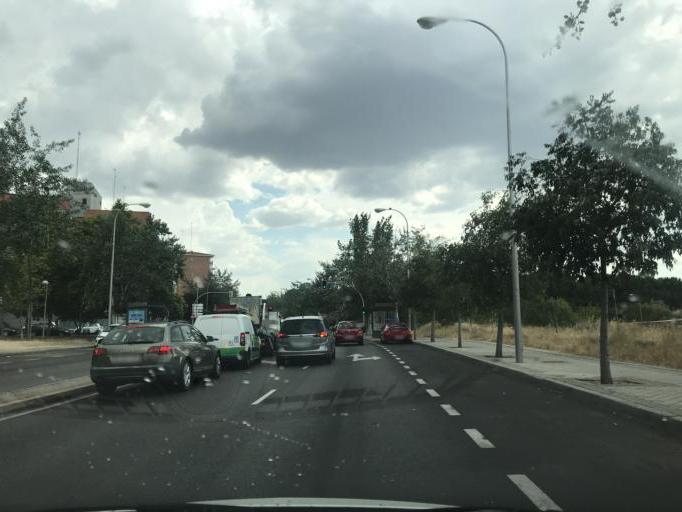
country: ES
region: Madrid
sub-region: Provincia de Madrid
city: Hortaleza
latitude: 40.4774
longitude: -3.6539
